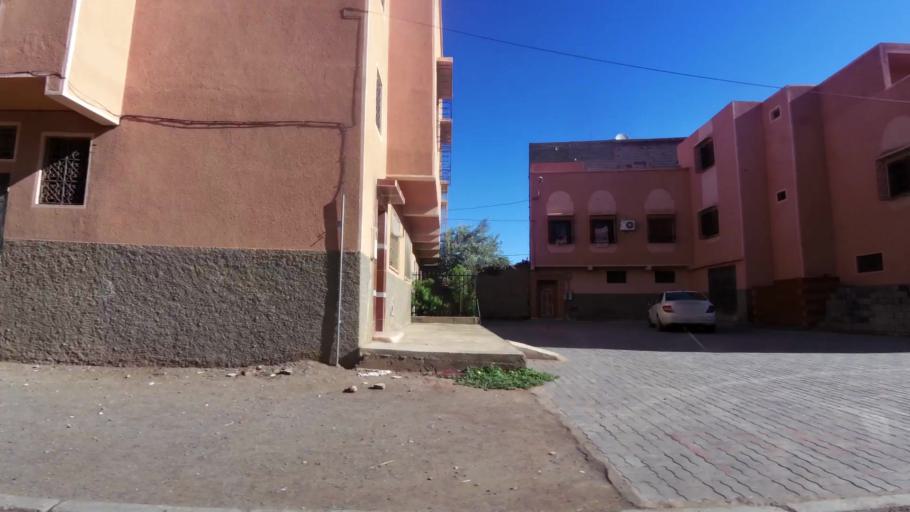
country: MA
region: Marrakech-Tensift-Al Haouz
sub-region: Marrakech
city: Marrakesh
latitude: 31.5951
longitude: -8.0253
